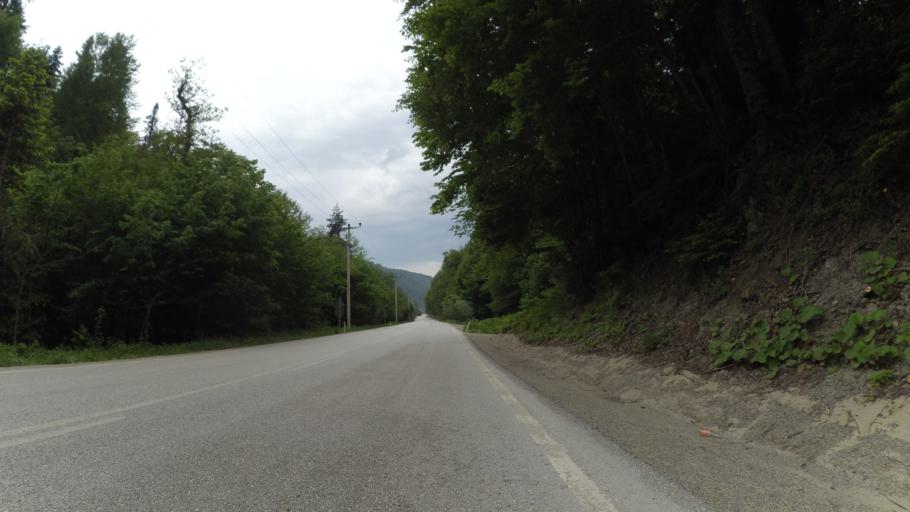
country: TR
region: Duzce
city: Kaynasli
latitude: 40.6456
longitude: 31.3581
